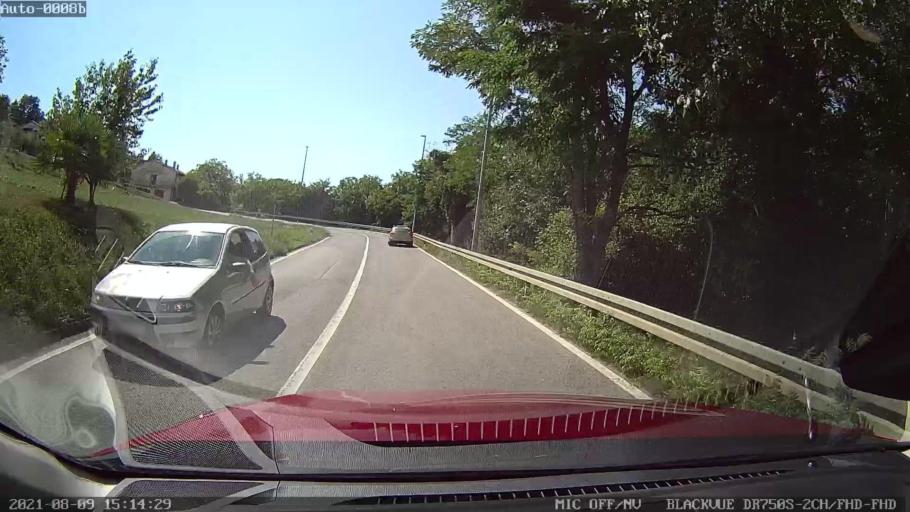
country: HR
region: Istarska
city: Pazin
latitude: 45.2399
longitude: 13.9233
